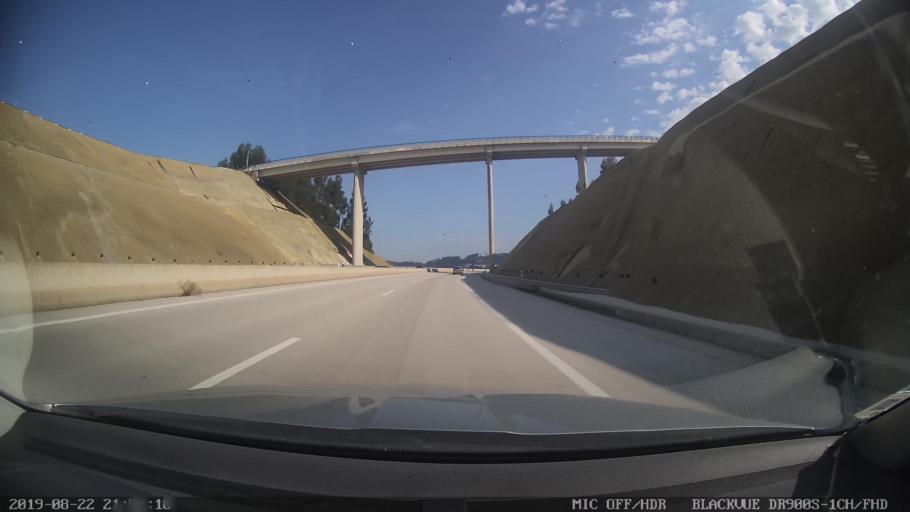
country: PT
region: Coimbra
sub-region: Coimbra
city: Coimbra
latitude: 40.1679
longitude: -8.3785
